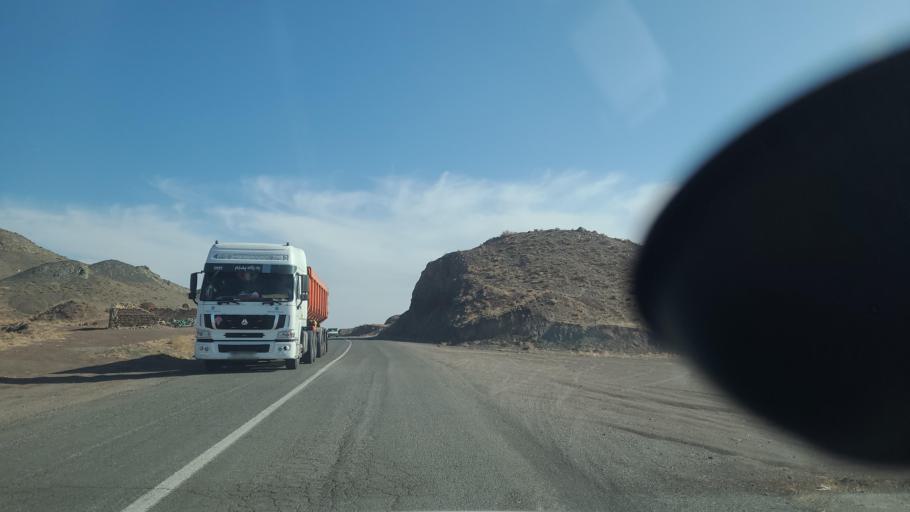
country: IR
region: Razavi Khorasan
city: Fariman
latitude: 35.5943
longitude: 59.7146
